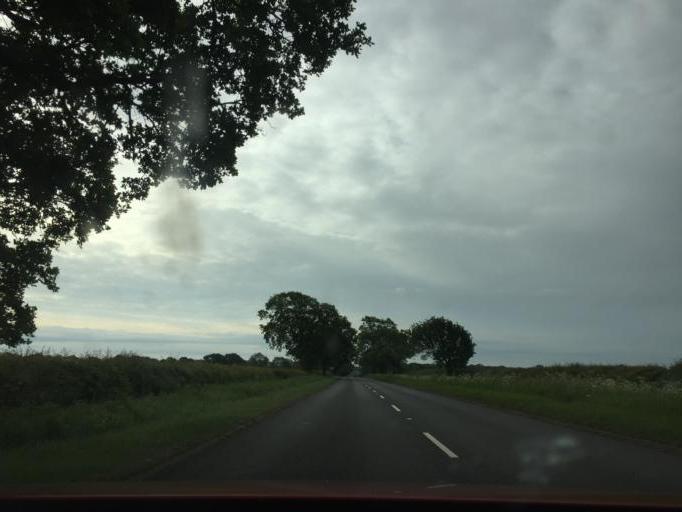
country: GB
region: England
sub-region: Leicestershire
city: Hinckley
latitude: 52.4840
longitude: -1.3389
